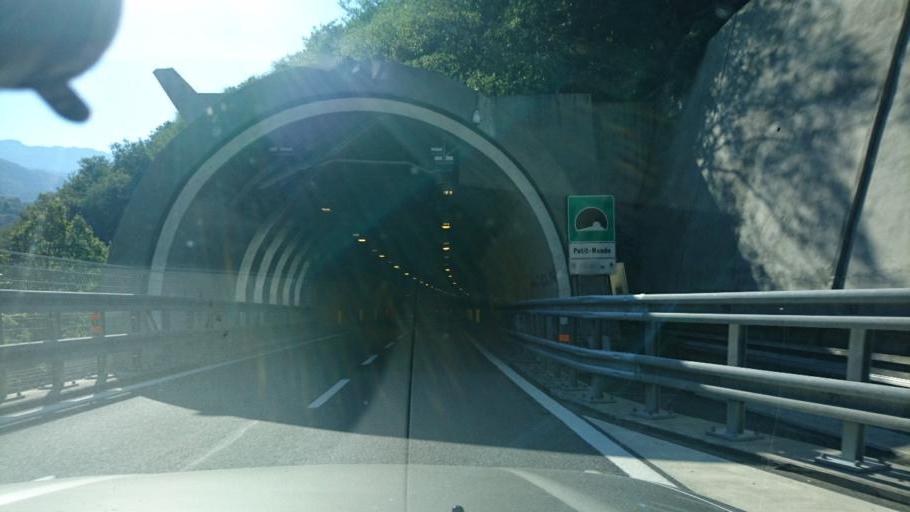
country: IT
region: Aosta Valley
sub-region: Valle d'Aosta
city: Saint-Vincent
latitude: 45.7361
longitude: 7.6560
